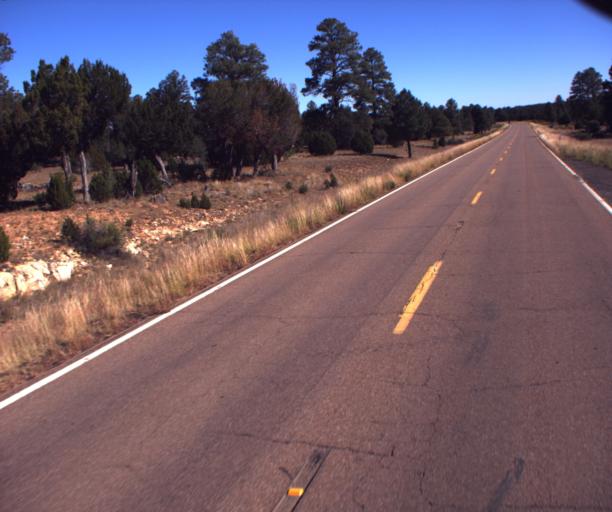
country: US
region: Arizona
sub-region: Navajo County
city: Heber-Overgaard
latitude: 34.4335
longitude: -110.5407
